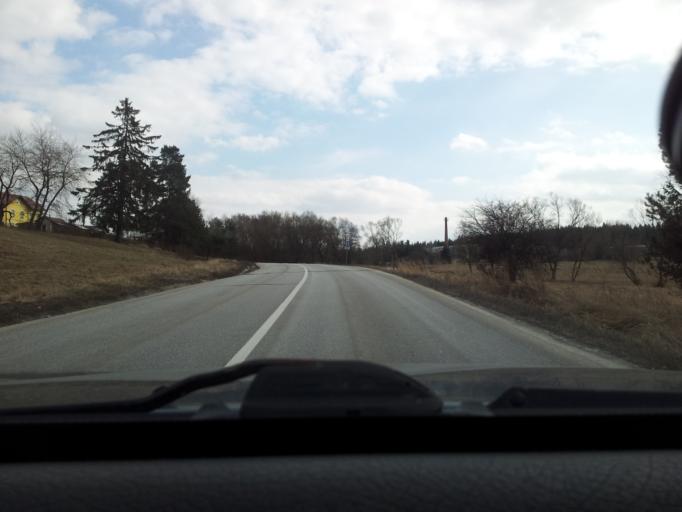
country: SK
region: Banskobystricky
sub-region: Okres Ziar nad Hronom
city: Kremnica
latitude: 48.7439
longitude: 18.9005
